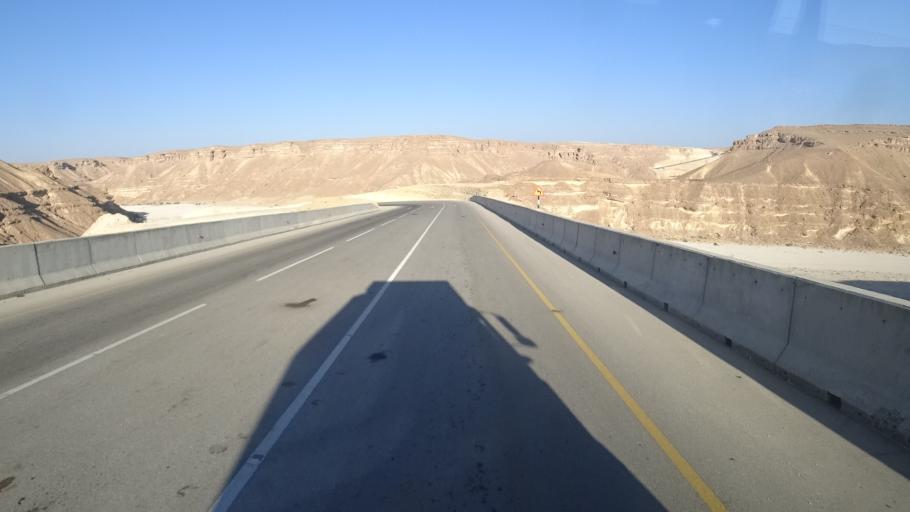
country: YE
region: Al Mahrah
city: Hawf
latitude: 17.0940
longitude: 53.0447
